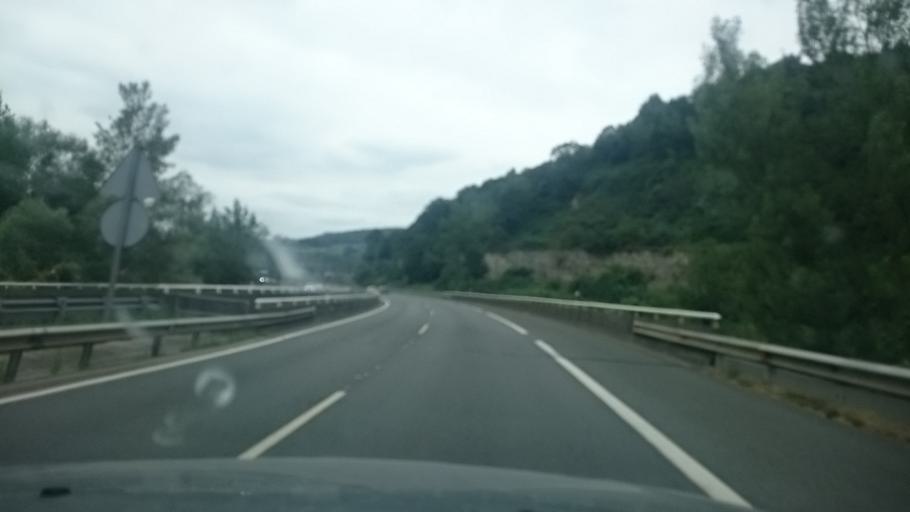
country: ES
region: Asturias
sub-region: Province of Asturias
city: Castandiello
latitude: 43.3027
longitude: -5.8509
